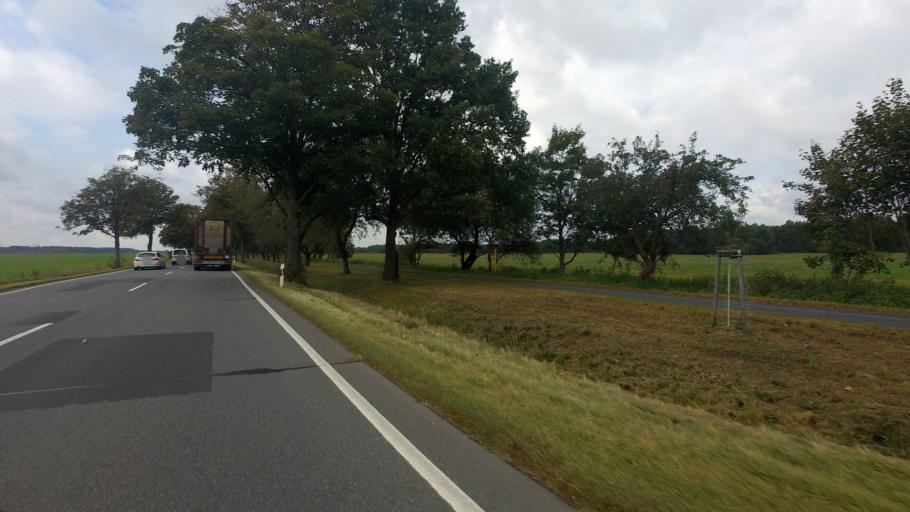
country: DE
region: Brandenburg
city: Schwarzheide
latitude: 51.4709
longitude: 13.8415
